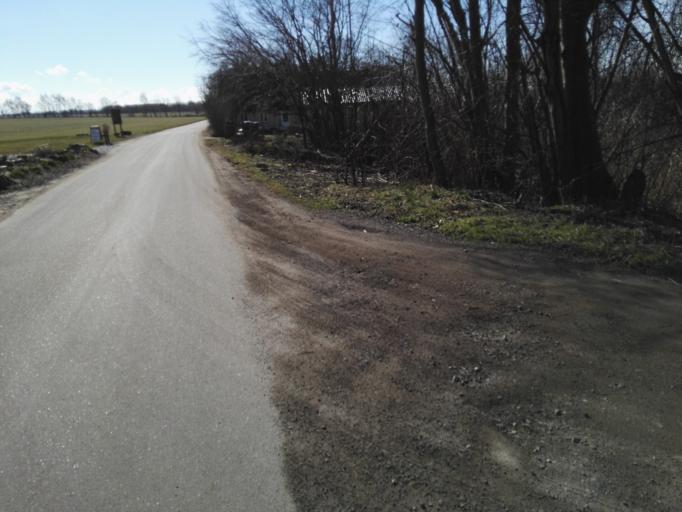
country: DK
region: Zealand
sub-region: Holbaek Kommune
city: Holbaek
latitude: 55.7852
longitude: 11.7956
